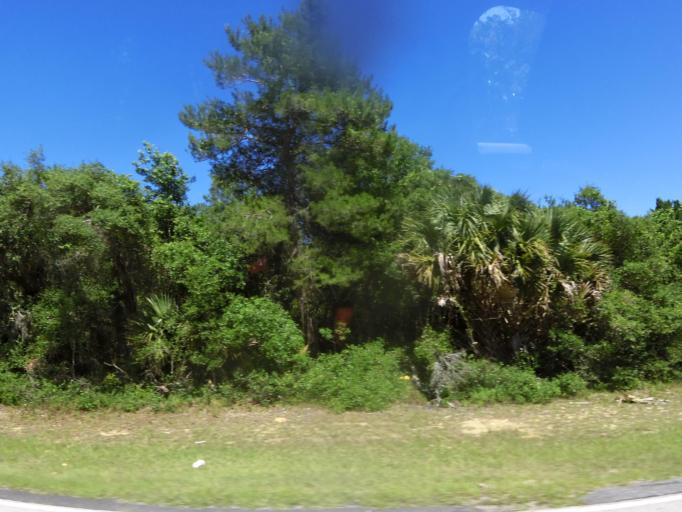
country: US
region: Florida
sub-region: Flagler County
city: Flagler Beach
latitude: 29.4125
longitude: -81.1482
